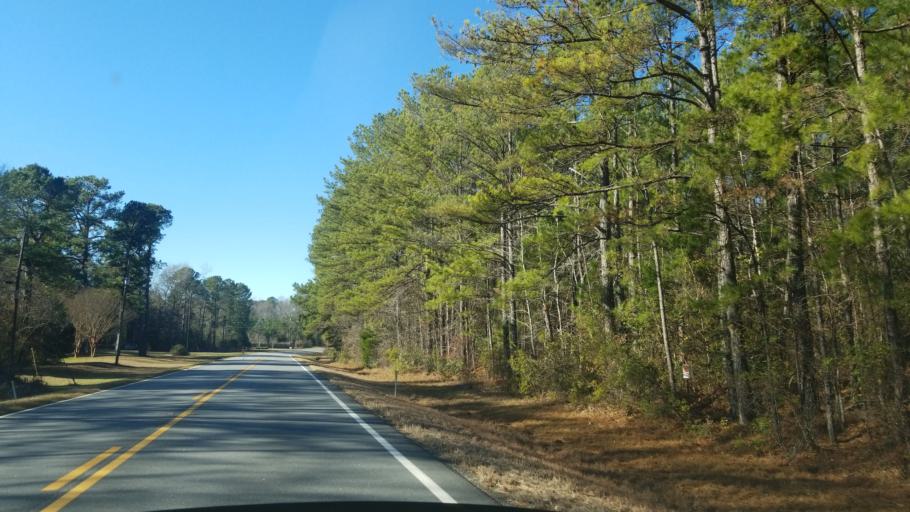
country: US
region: Georgia
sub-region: Harris County
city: Hamilton
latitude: 32.6699
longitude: -84.9014
